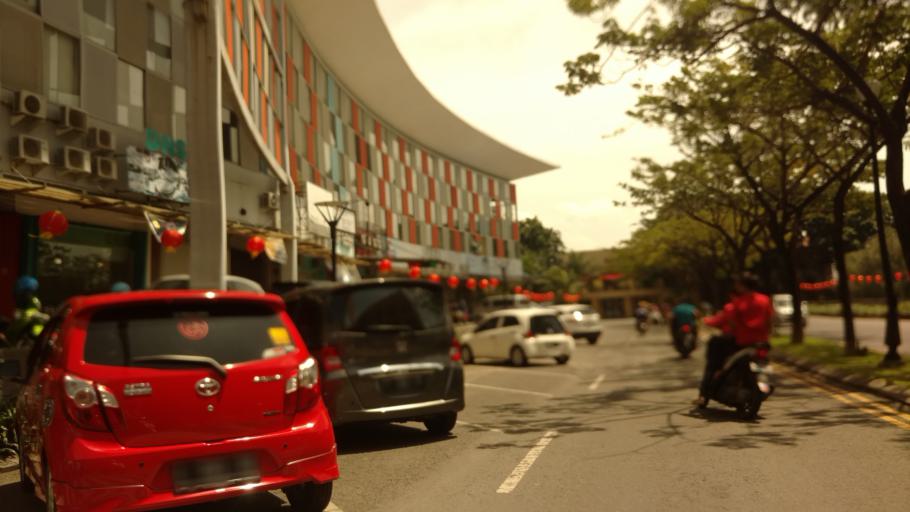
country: ID
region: East Java
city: Driyorejo
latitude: -7.2851
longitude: 112.6566
